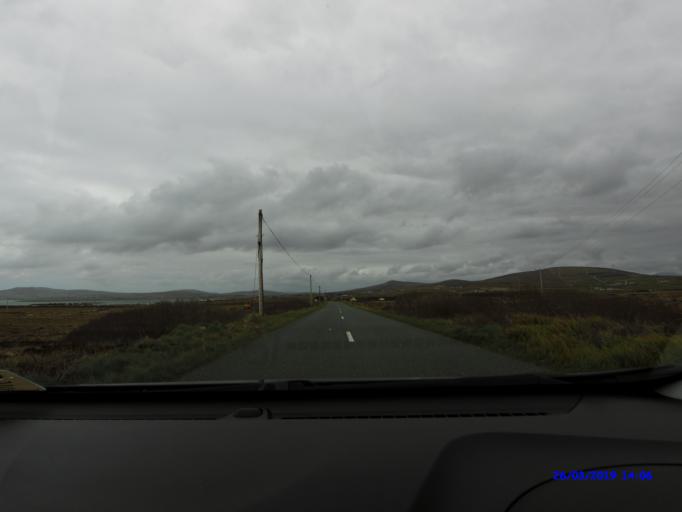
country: IE
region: Connaught
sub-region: Maigh Eo
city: Belmullet
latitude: 54.2071
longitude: -9.9257
